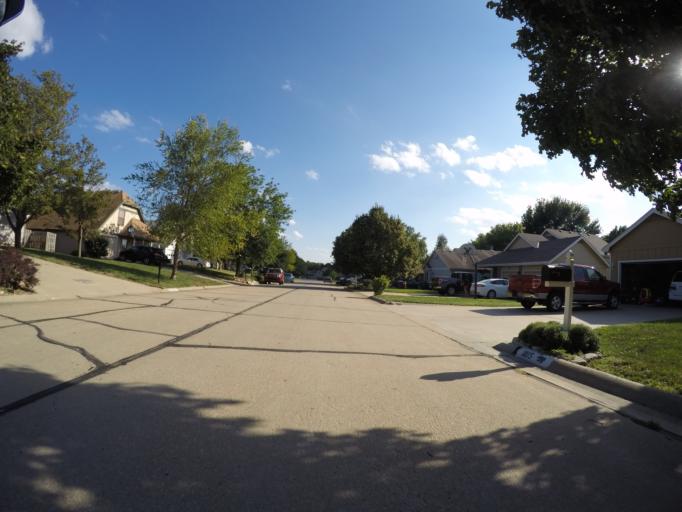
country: US
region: Kansas
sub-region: Riley County
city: Manhattan
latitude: 39.2006
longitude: -96.6295
